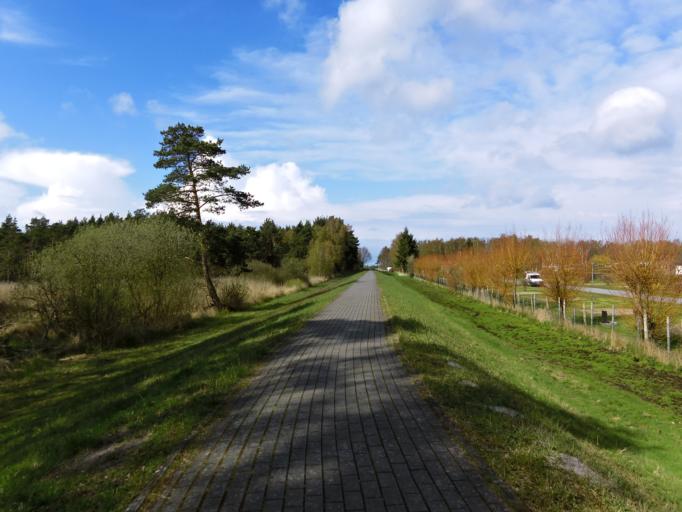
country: DE
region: Mecklenburg-Vorpommern
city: Zingst
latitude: 54.4382
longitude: 12.6597
